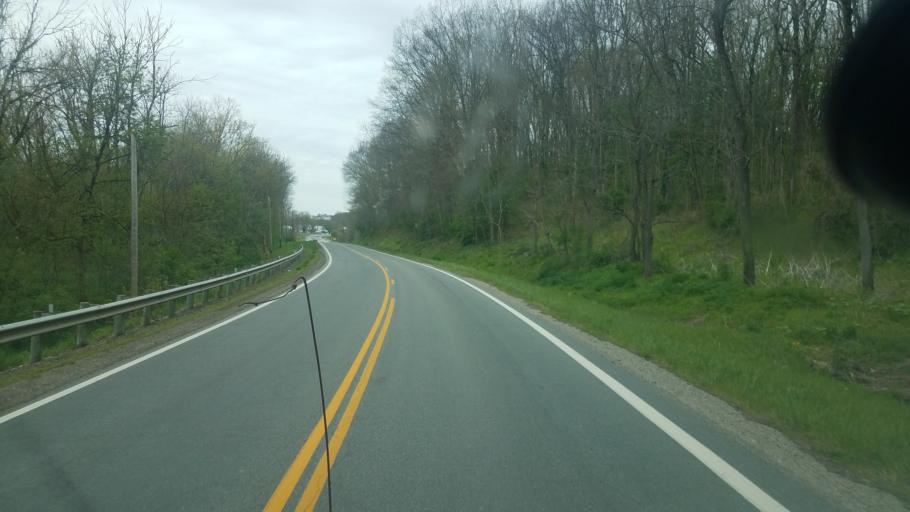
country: US
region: Ohio
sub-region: Knox County
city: Danville
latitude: 40.4073
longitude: -82.3161
